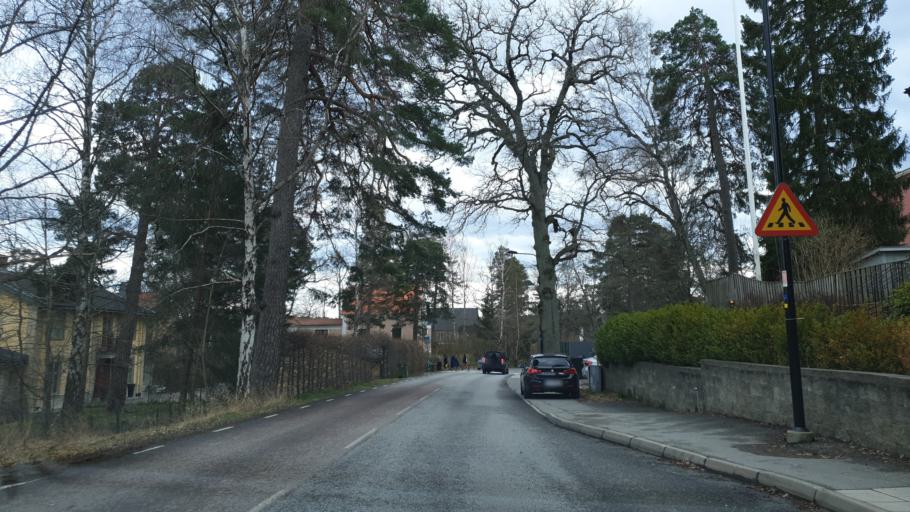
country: SE
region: Stockholm
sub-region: Nacka Kommun
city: Nacka
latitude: 59.3053
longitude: 18.2011
